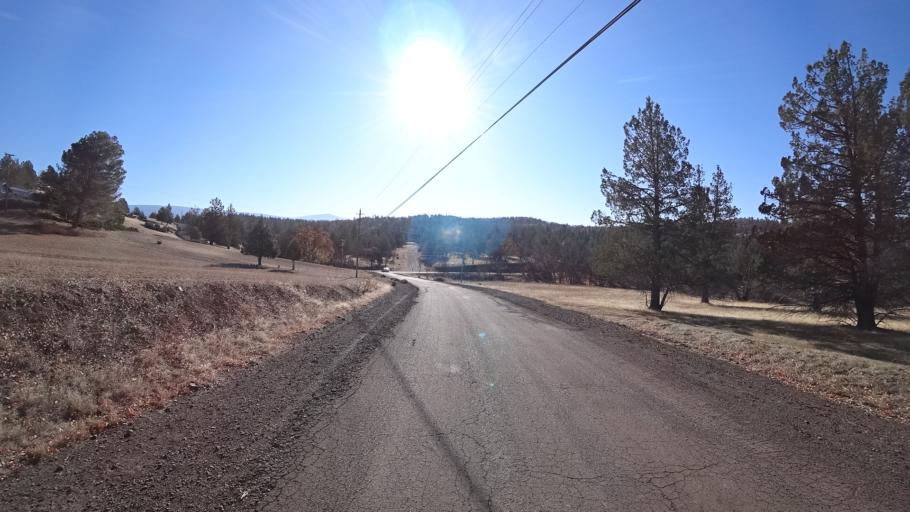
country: US
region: California
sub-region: Siskiyou County
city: Montague
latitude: 41.9136
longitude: -122.4332
